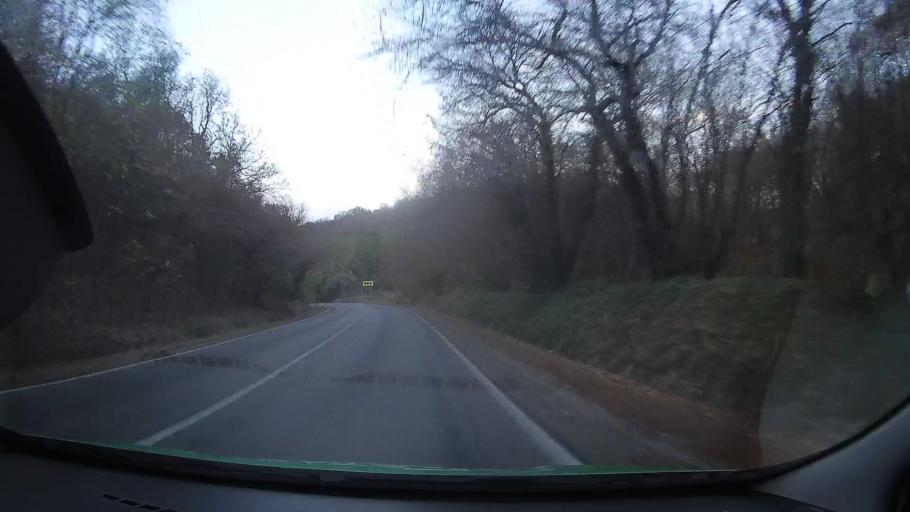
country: RO
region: Constanta
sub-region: Comuna Baneasa
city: Baneasa
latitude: 44.0932
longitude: 27.6534
